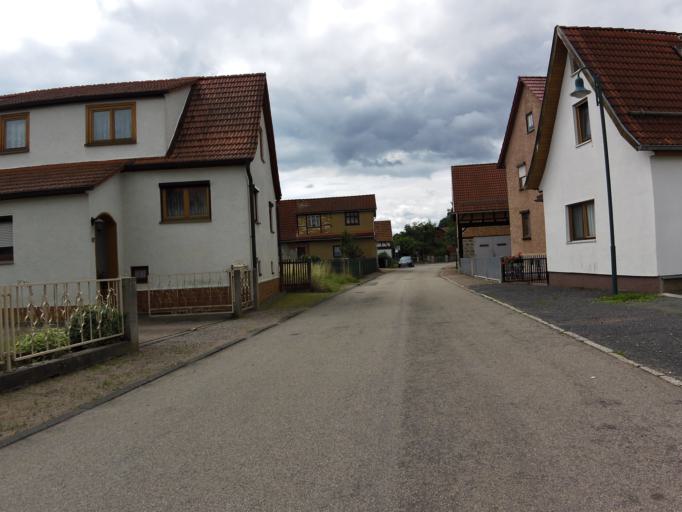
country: DE
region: Thuringia
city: Fambach
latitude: 50.7183
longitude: 10.4004
